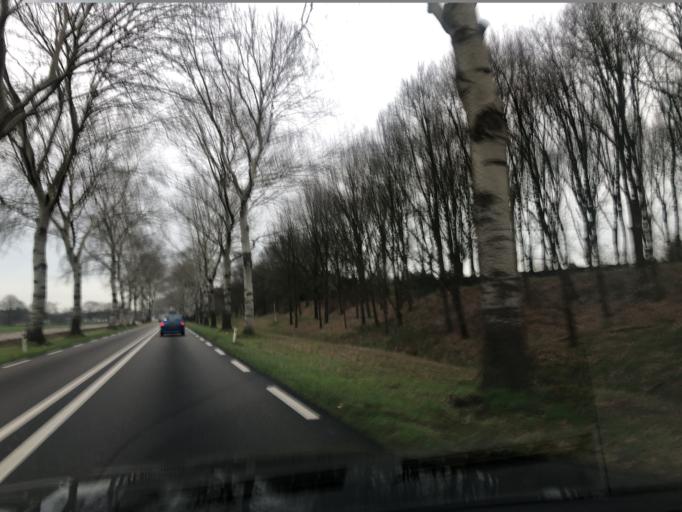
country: NL
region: North Brabant
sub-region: Gemeente Uden
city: Uden
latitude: 51.6749
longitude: 5.6312
